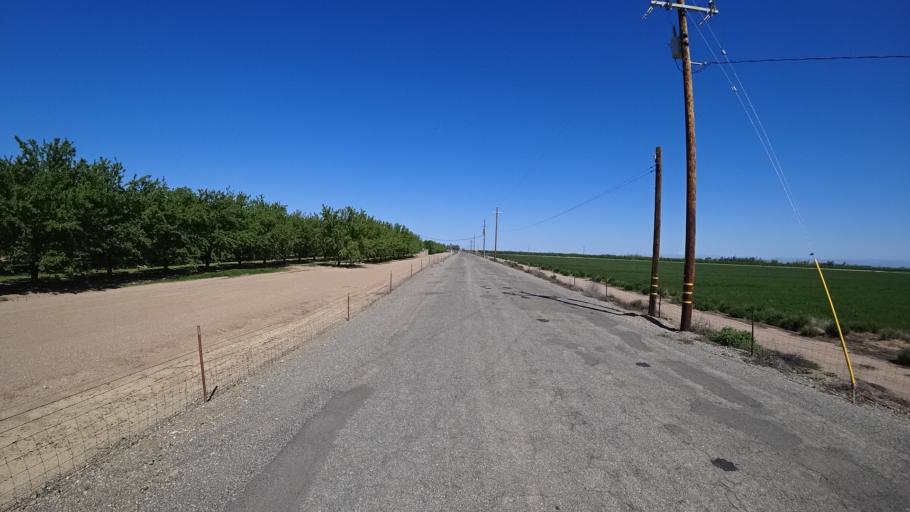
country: US
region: California
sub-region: Glenn County
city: Orland
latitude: 39.6651
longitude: -122.2345
